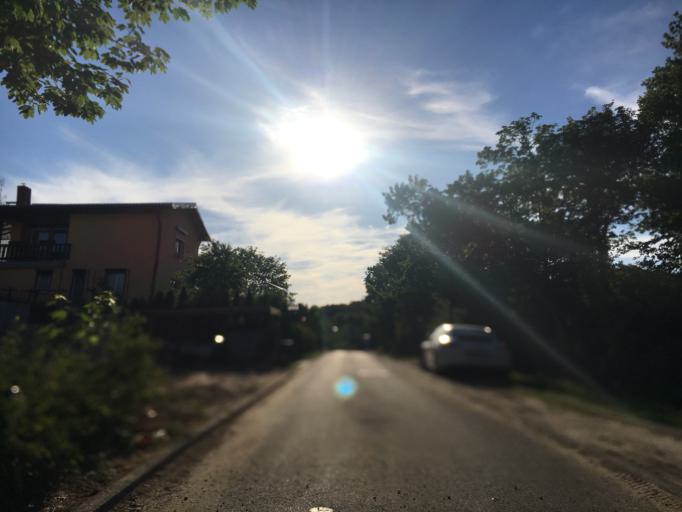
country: DE
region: Brandenburg
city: Potsdam
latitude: 52.4270
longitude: 13.0647
